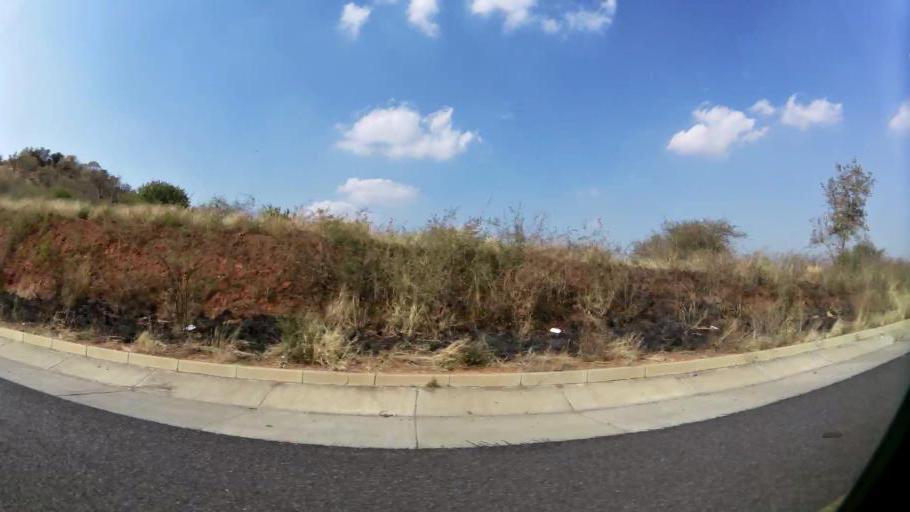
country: ZA
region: North-West
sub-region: Bojanala Platinum District Municipality
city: Rustenburg
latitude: -25.5717
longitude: 27.1400
